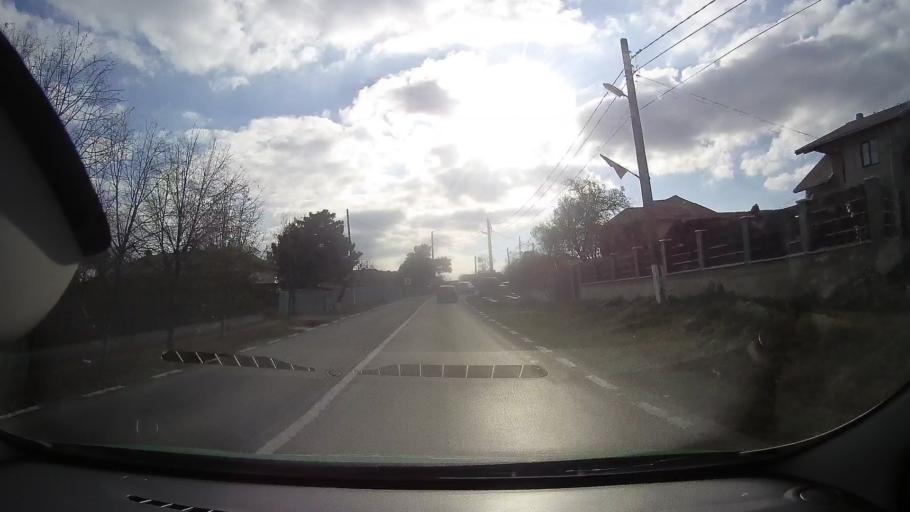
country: RO
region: Tulcea
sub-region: Comuna Topolog
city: Topolog
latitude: 44.8745
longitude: 28.3734
